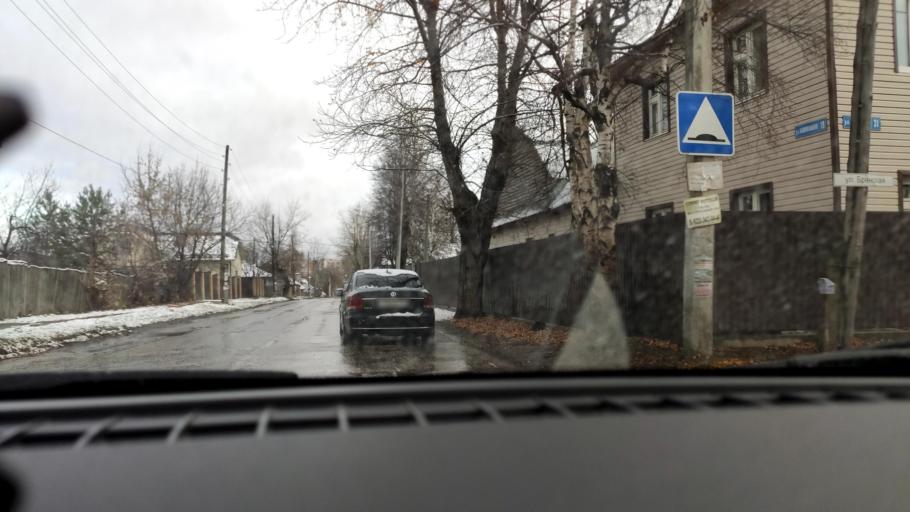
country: RU
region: Perm
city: Perm
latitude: 58.0189
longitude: 56.3146
